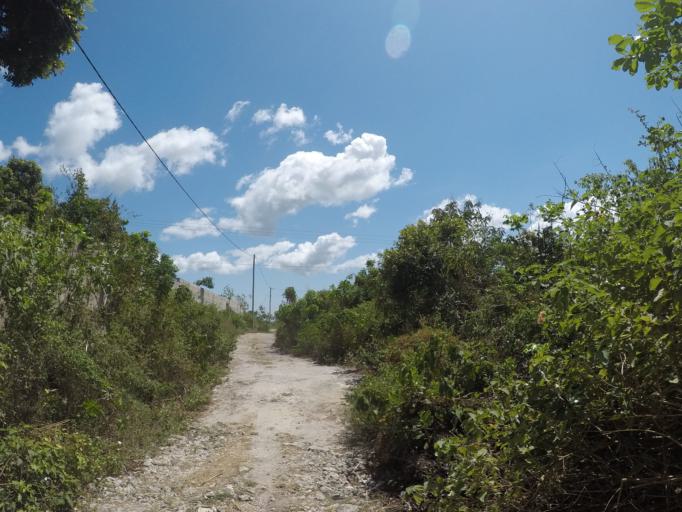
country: TZ
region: Zanzibar Central/South
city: Nganane
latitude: -6.2758
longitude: 39.5343
